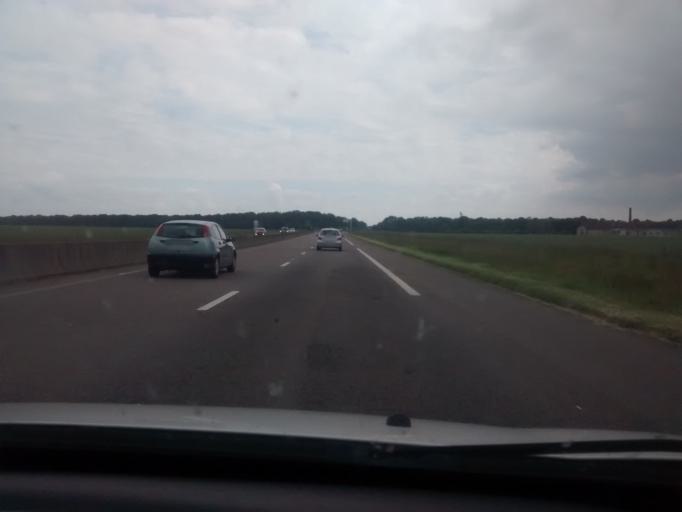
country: FR
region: Ile-de-France
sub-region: Departement des Yvelines
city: Ablis
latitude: 48.5502
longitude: 1.8300
